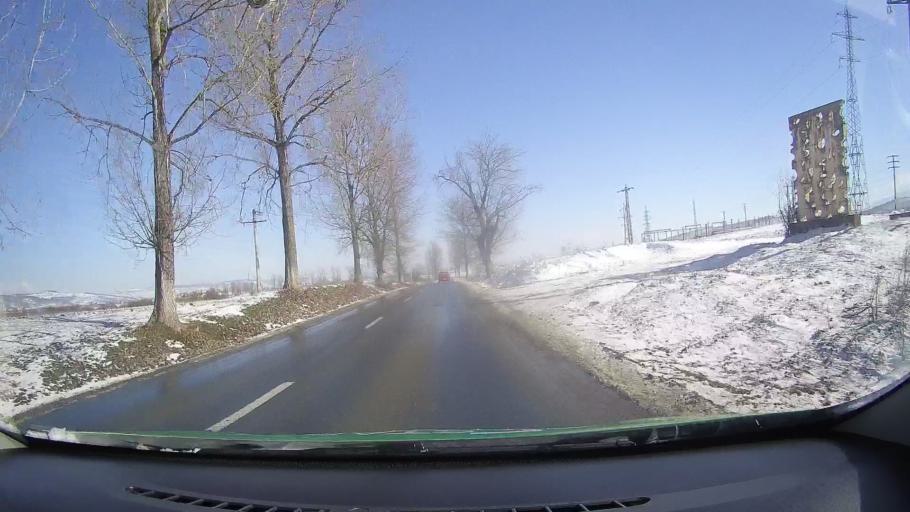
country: RO
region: Sibiu
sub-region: Comuna Avrig
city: Marsa
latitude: 45.7037
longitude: 24.3647
